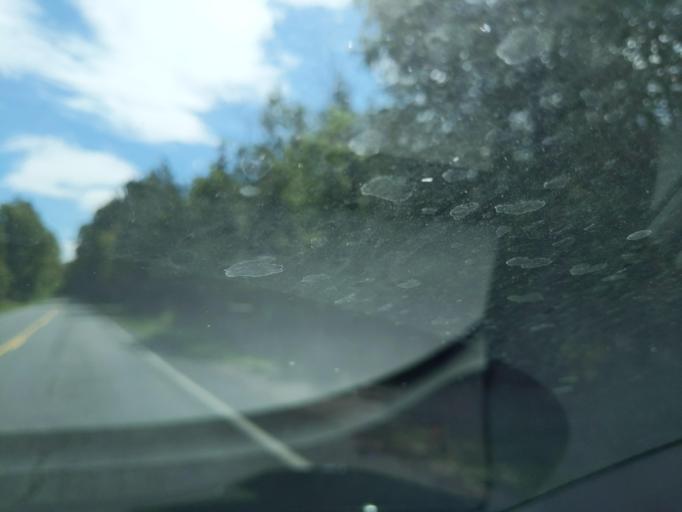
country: US
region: Michigan
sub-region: Antrim County
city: Bellaire
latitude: 45.0303
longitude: -85.2957
